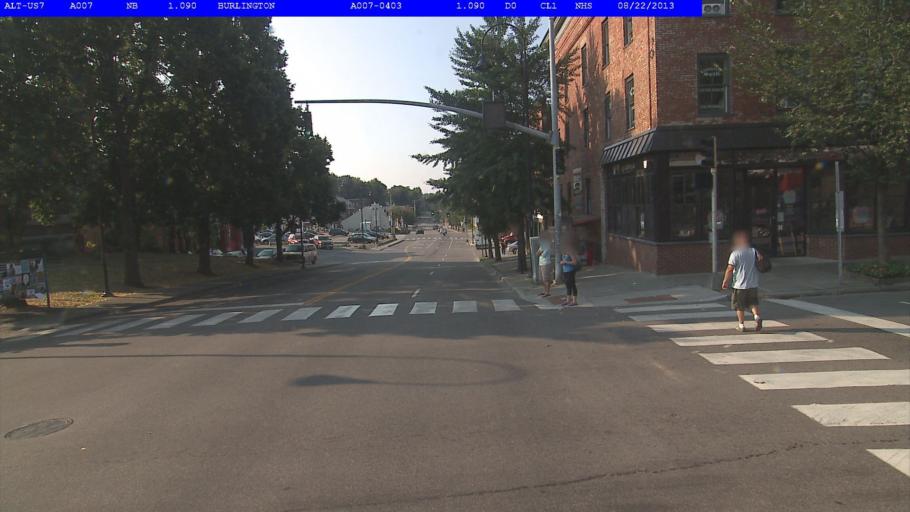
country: US
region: Vermont
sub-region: Chittenden County
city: Burlington
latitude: 44.4772
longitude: -73.2111
